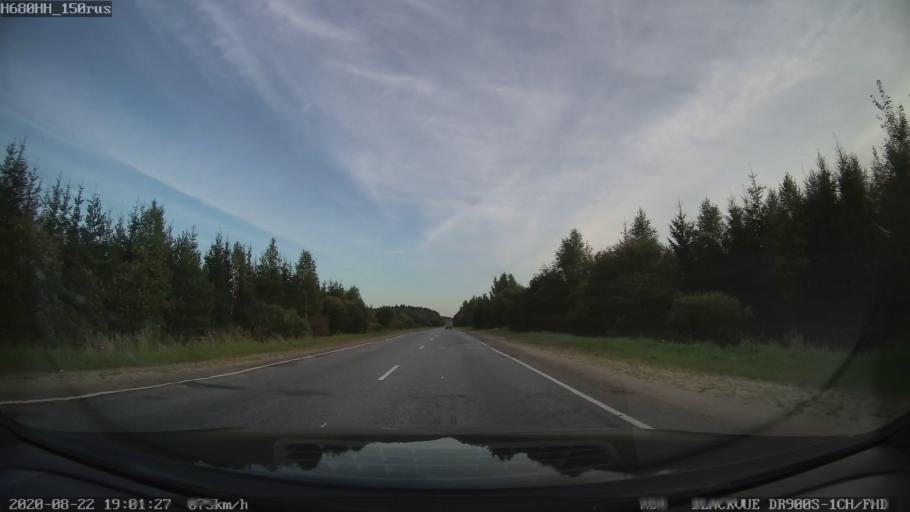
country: RU
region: Tverskaya
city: Vasil'yevskiy Mokh
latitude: 57.1191
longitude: 36.1150
